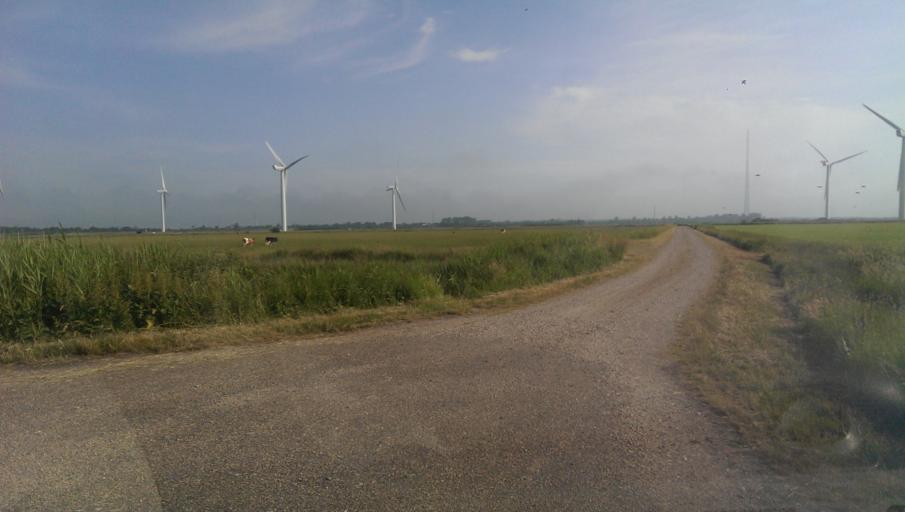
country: DK
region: South Denmark
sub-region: Esbjerg Kommune
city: Tjaereborg
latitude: 55.4421
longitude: 8.5872
